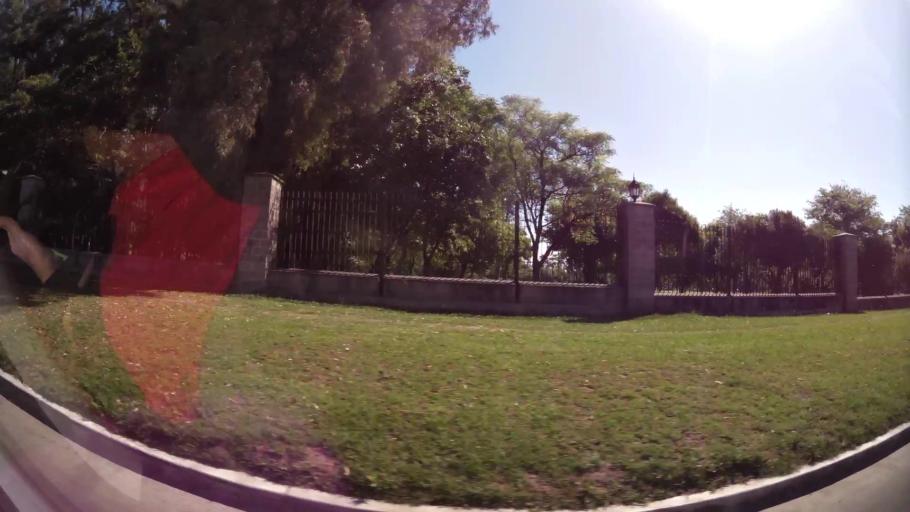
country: AR
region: Buenos Aires
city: Santa Catalina - Dique Lujan
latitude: -34.4918
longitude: -58.6982
